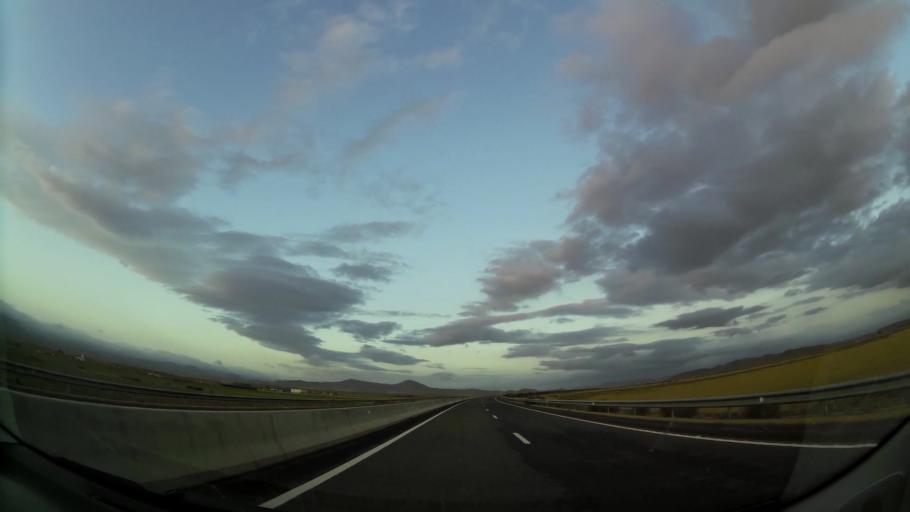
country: MA
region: Oriental
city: Taourirt
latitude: 34.6052
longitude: -2.7573
